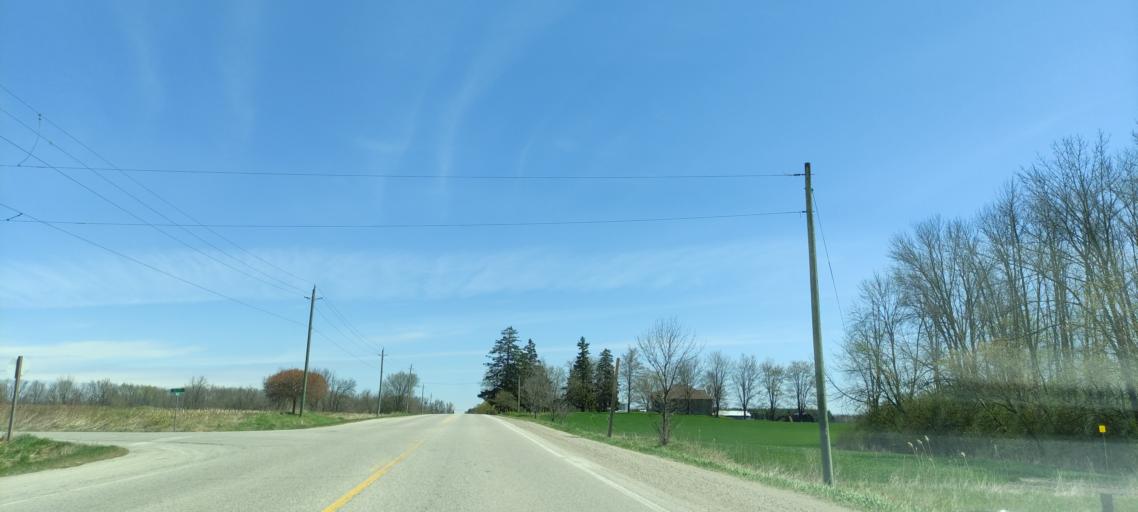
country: CA
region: Ontario
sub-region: Wellington County
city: Guelph
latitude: 43.5795
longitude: -80.3633
